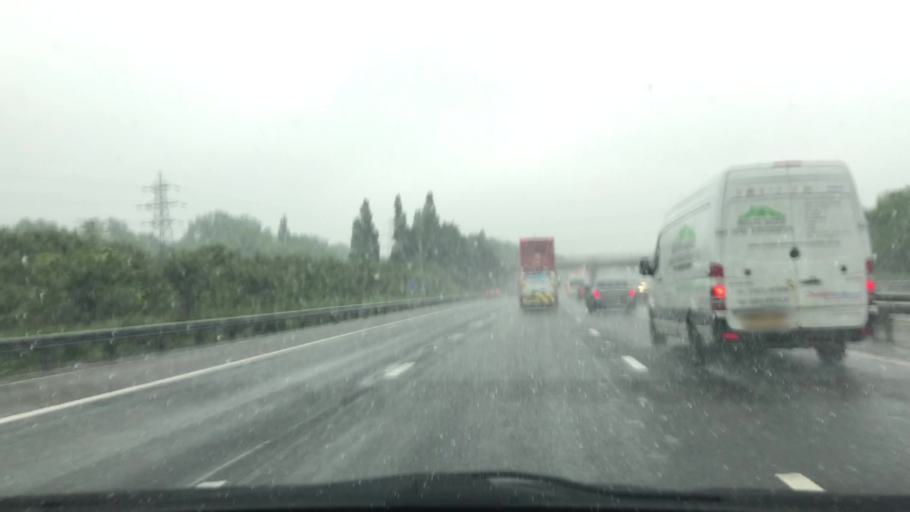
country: GB
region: England
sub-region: Central Bedfordshire
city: Chalton
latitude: 51.9405
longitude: -0.4979
